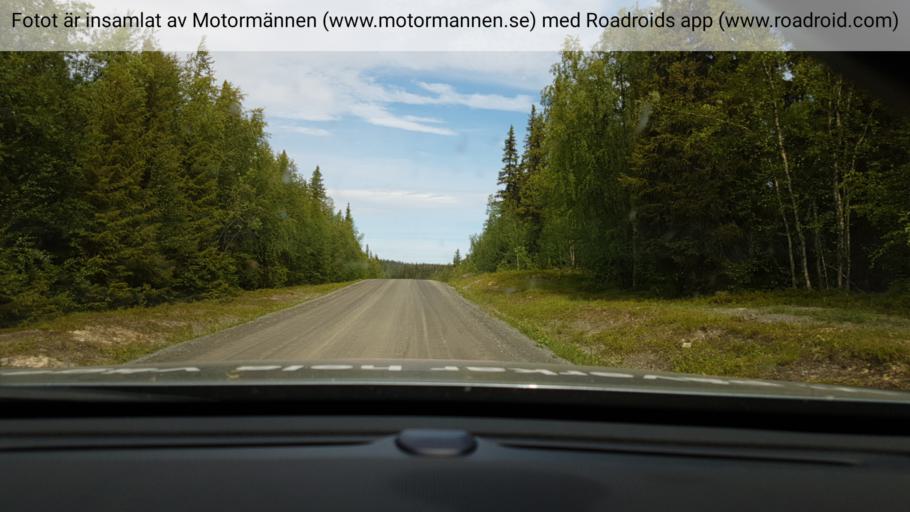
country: SE
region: Vaesterbotten
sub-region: Vilhelmina Kommun
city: Sjoberg
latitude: 65.1710
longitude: 16.3562
